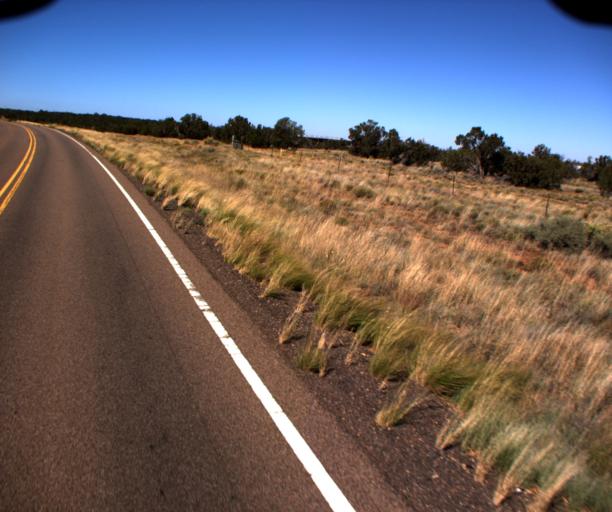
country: US
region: Arizona
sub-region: Navajo County
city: Taylor
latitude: 34.4826
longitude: -110.3052
